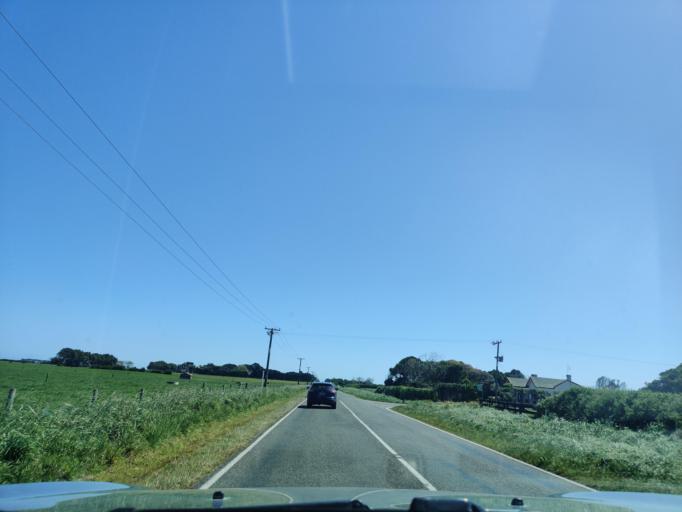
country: NZ
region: Taranaki
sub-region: South Taranaki District
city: Hawera
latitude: -39.5499
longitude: 174.1147
